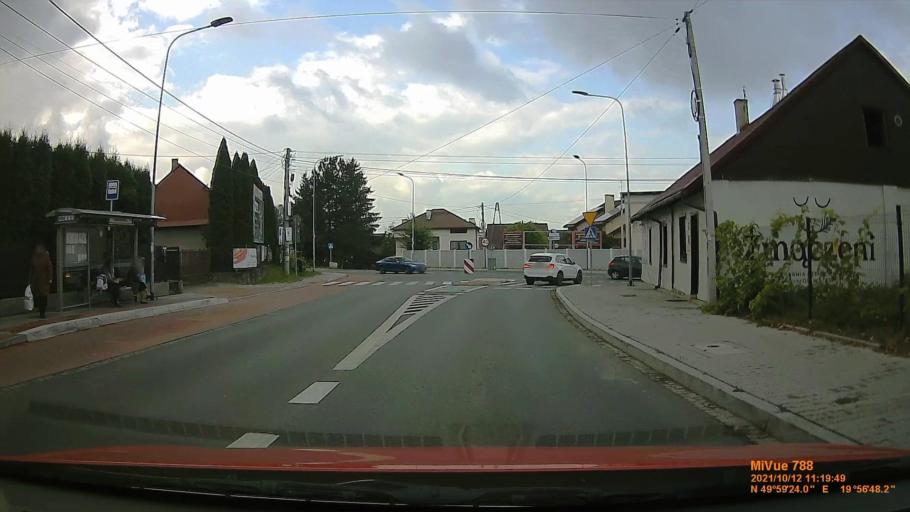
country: PL
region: Lesser Poland Voivodeship
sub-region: Powiat krakowski
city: Wrzasowice
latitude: 49.9900
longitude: 19.9466
